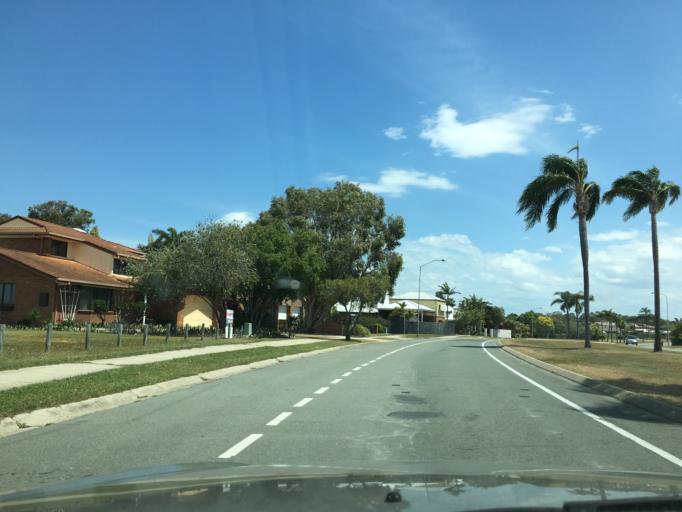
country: AU
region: Queensland
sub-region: Moreton Bay
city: Bongaree
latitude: -27.0820
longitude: 153.1362
